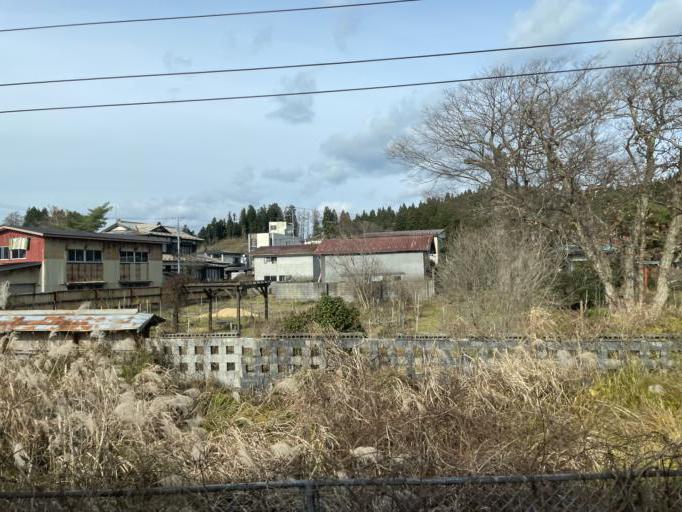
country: JP
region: Akita
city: Akita
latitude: 39.6512
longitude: 140.2223
